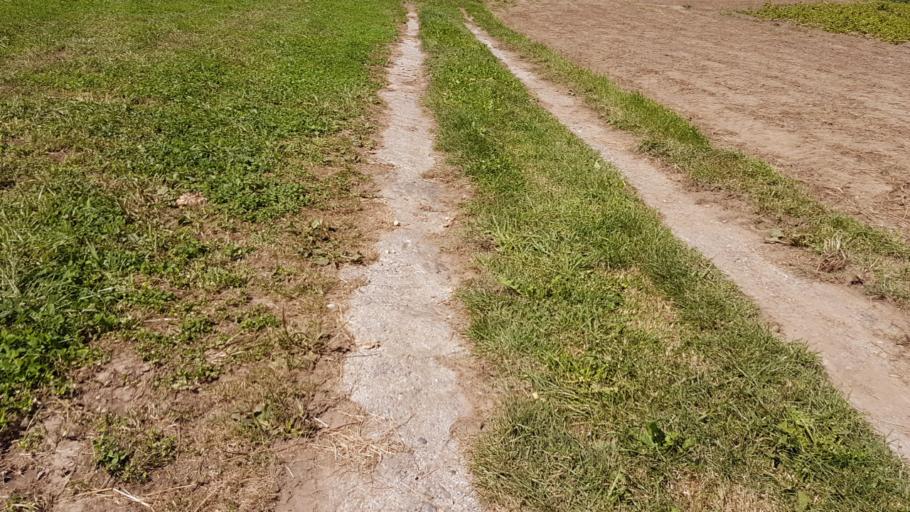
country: CH
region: Bern
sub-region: Bern-Mittelland District
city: Konolfingen
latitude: 46.8635
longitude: 7.6261
